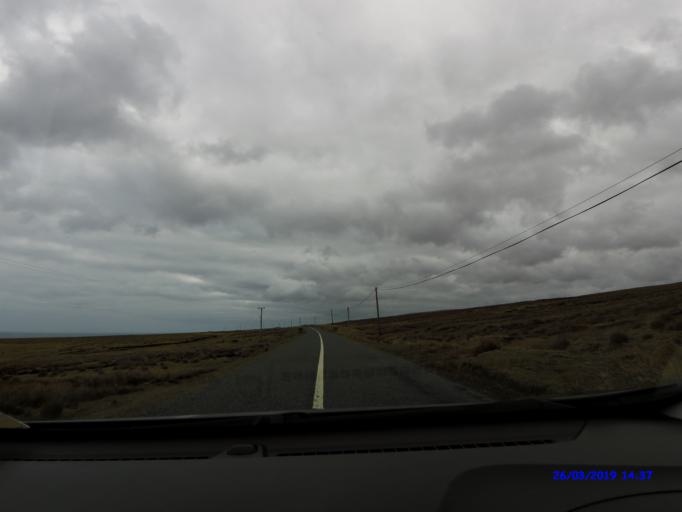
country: IE
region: Connaught
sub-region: Maigh Eo
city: Crossmolina
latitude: 54.3082
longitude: -9.5168
